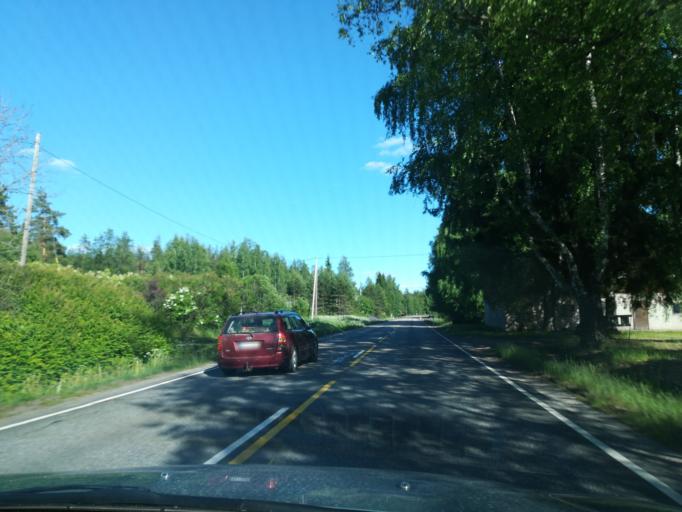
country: FI
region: South Karelia
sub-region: Imatra
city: Ruokolahti
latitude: 61.3724
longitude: 28.6675
